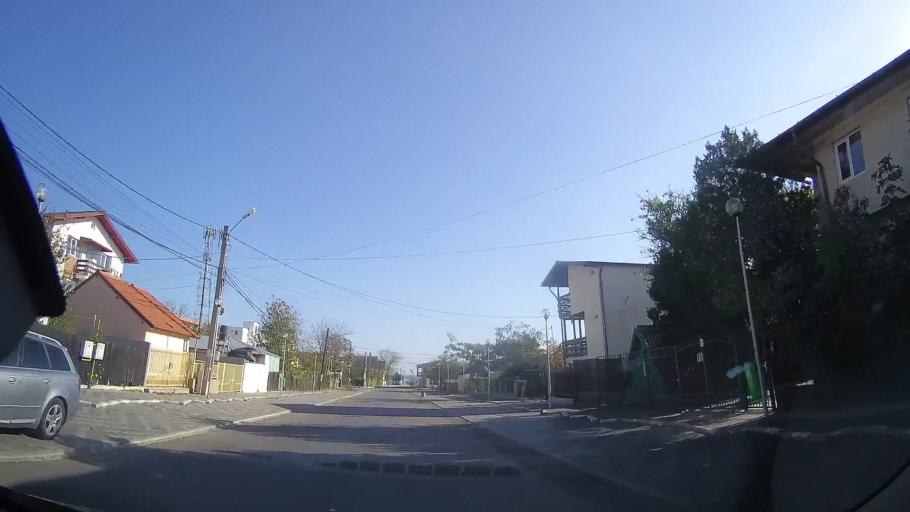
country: RO
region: Constanta
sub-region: Comuna Costinesti
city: Costinesti
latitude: 43.9535
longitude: 28.6355
